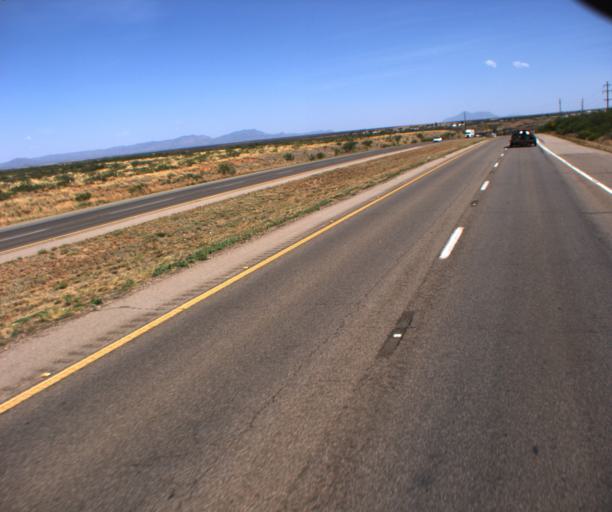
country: US
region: Arizona
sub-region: Cochise County
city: Huachuca City
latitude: 31.6540
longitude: -110.3456
